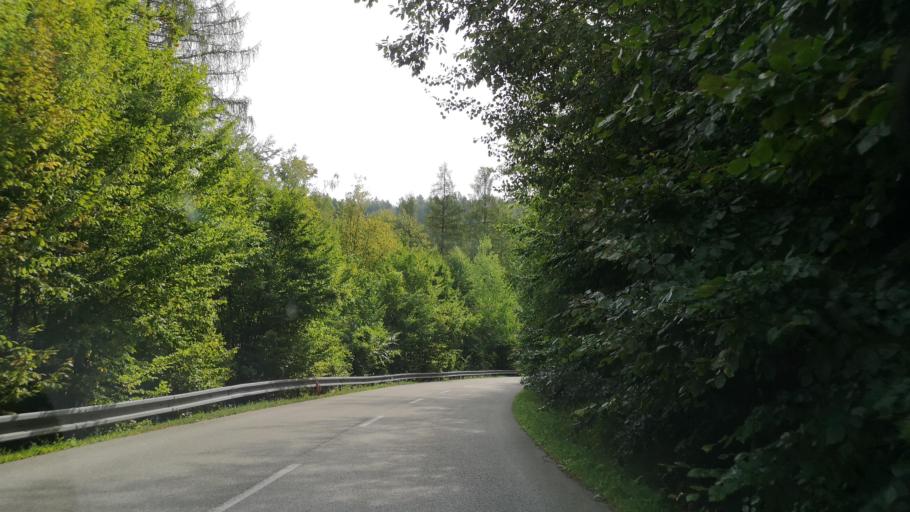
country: SK
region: Banskobystricky
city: Tisovec
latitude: 48.5830
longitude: 20.0099
